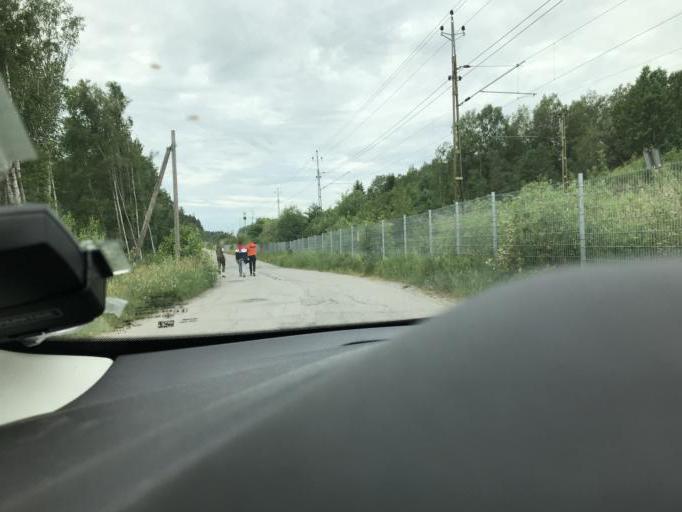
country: SE
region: Stockholm
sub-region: Botkyrka Kommun
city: Varsta
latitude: 59.1969
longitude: 17.7976
